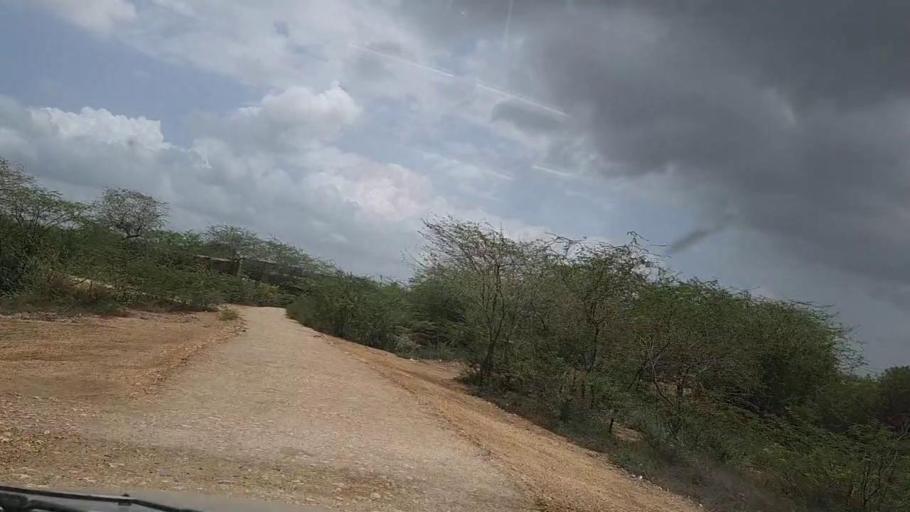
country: PK
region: Sindh
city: Thatta
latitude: 24.6203
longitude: 68.0262
